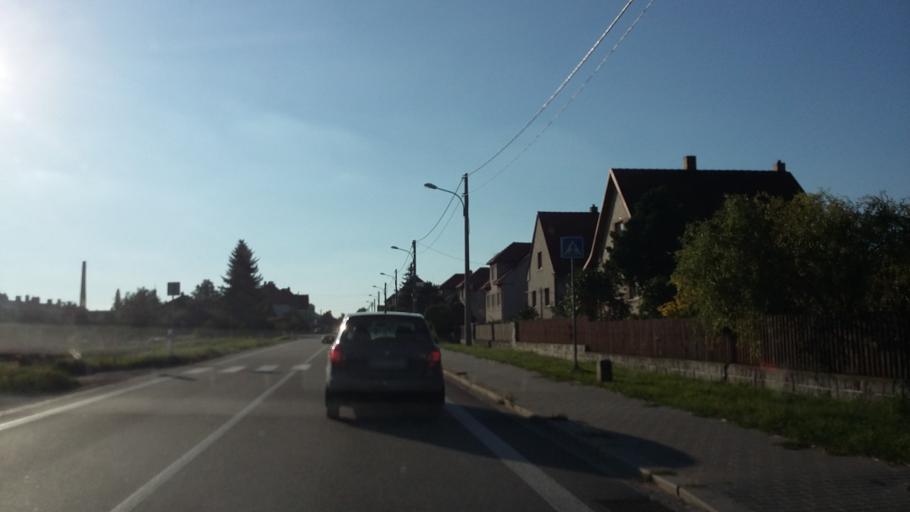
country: CZ
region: Vysocina
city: Merin
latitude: 49.3890
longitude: 15.8969
